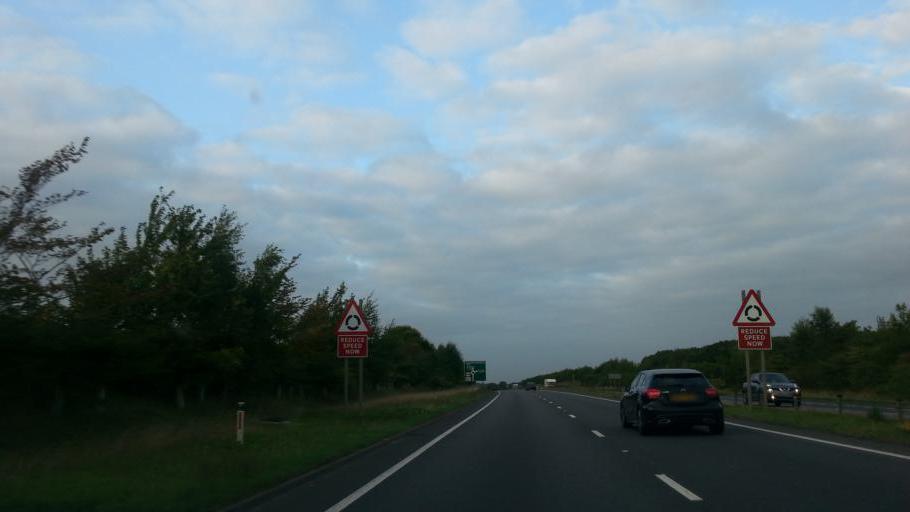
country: GB
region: England
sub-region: Northamptonshire
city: Brackley
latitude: 51.9916
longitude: -1.1656
